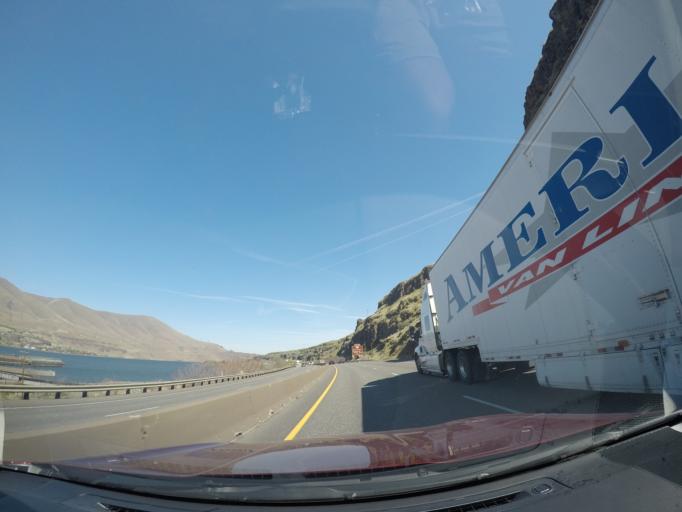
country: US
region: Washington
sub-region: Klickitat County
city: Dallesport
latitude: 45.6435
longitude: -120.9809
